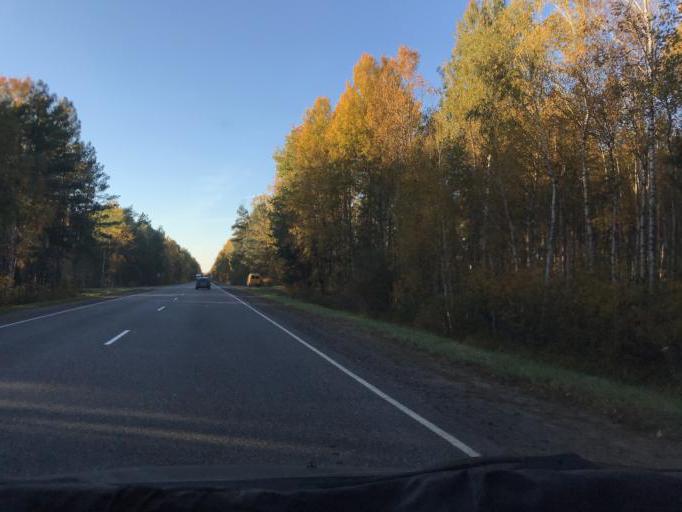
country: BY
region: Gomel
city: Pyetrykaw
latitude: 52.2491
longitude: 28.3702
